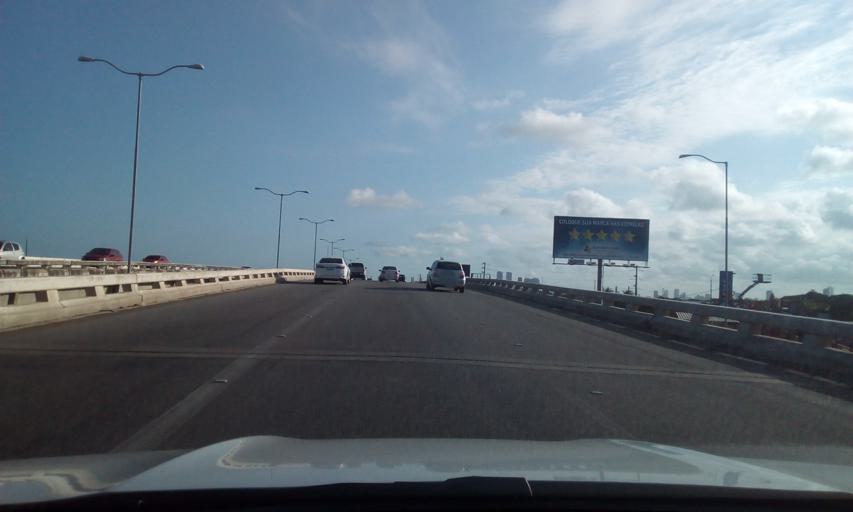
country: BR
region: Pernambuco
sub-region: Olinda
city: Olinda
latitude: -8.0176
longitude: -34.8605
